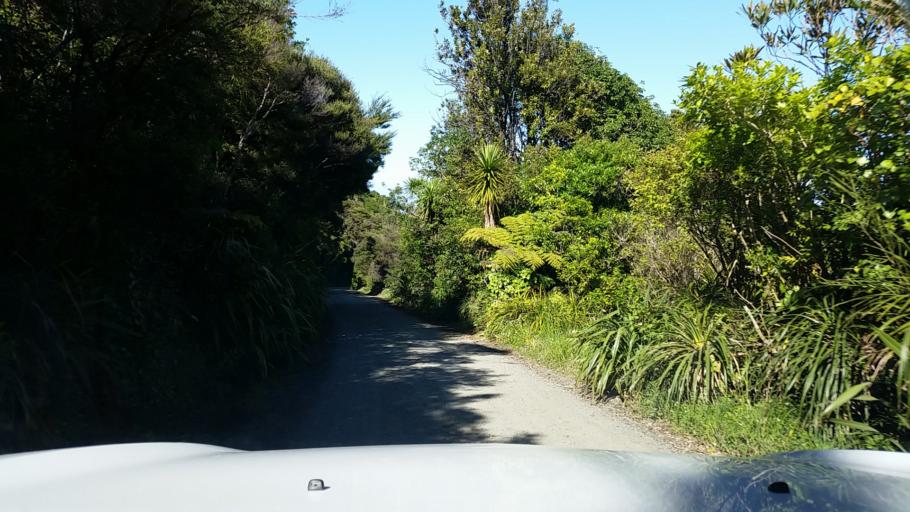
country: NZ
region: Auckland
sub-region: Auckland
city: Titirangi
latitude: -37.0270
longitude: 174.5292
